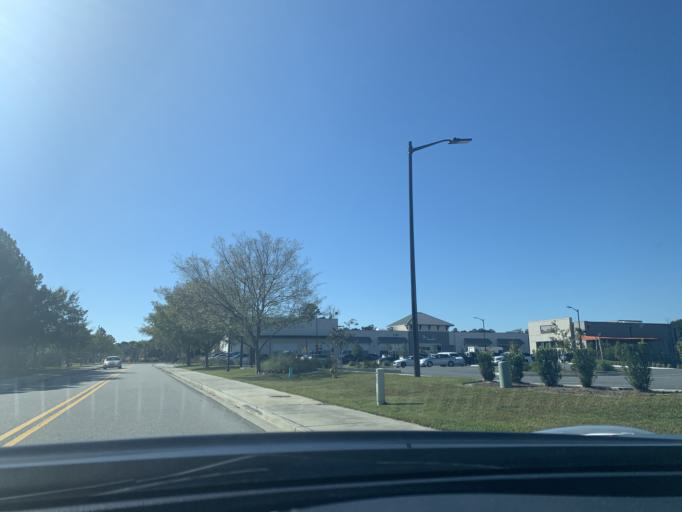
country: US
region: Georgia
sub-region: Chatham County
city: Pooler
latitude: 32.1354
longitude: -81.2561
